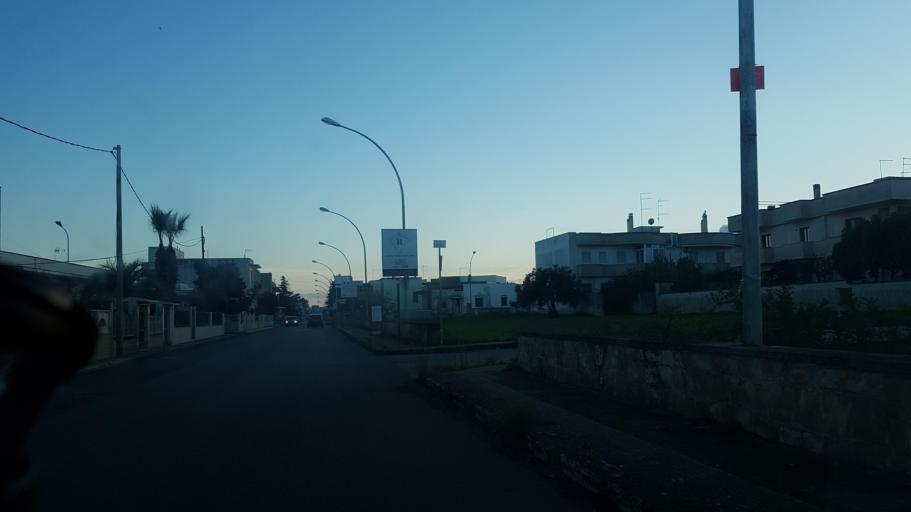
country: IT
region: Apulia
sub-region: Provincia di Brindisi
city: San Michele Salentino
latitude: 40.6372
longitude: 17.6320
